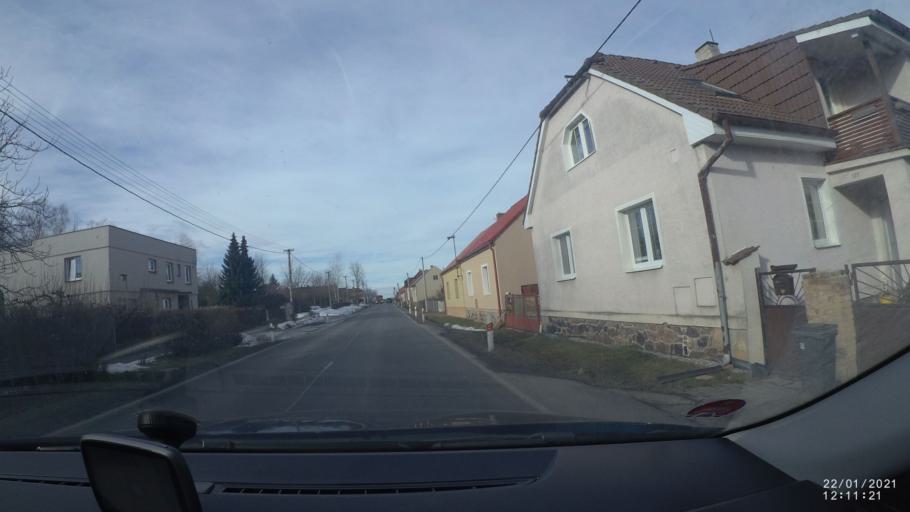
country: CZ
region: Plzensky
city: Dysina
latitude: 49.7509
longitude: 13.4917
